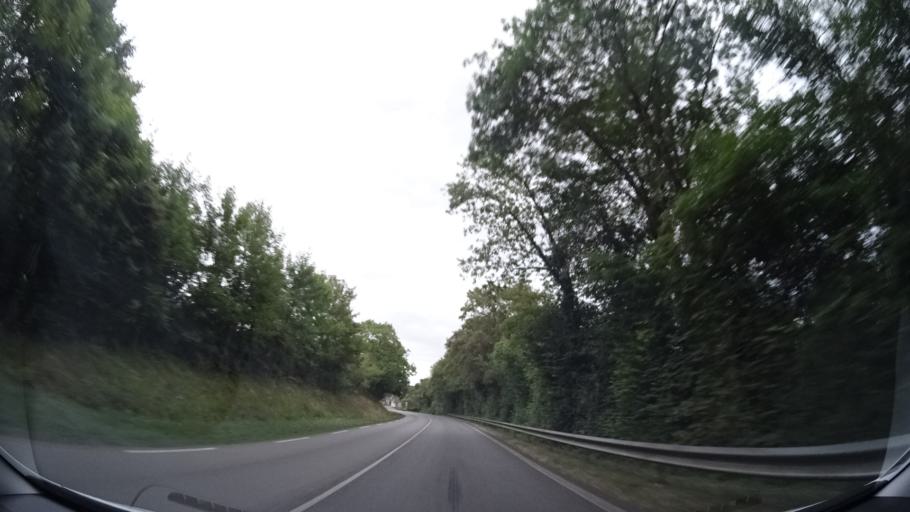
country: FR
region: Bourgogne
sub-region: Departement de l'Yonne
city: Charny
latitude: 47.9327
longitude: 3.0992
